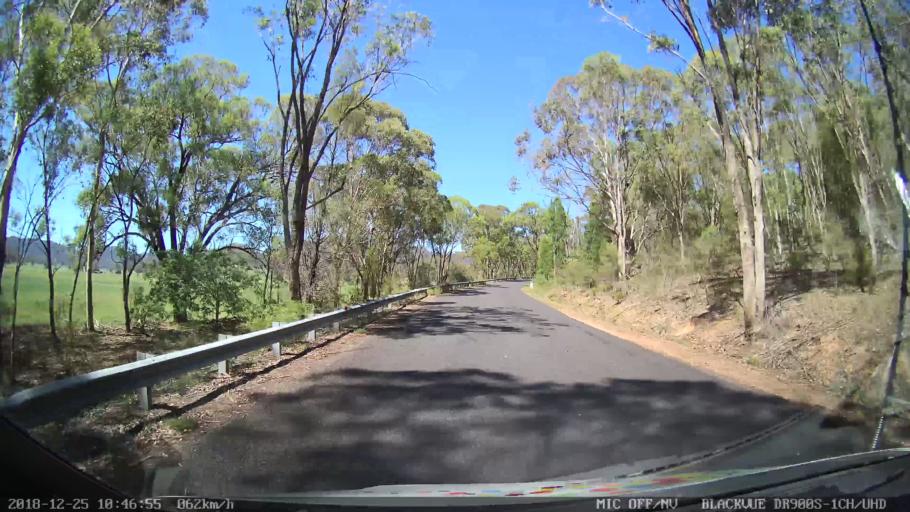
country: AU
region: New South Wales
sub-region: Upper Hunter Shire
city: Merriwa
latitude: -32.4448
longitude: 150.2805
